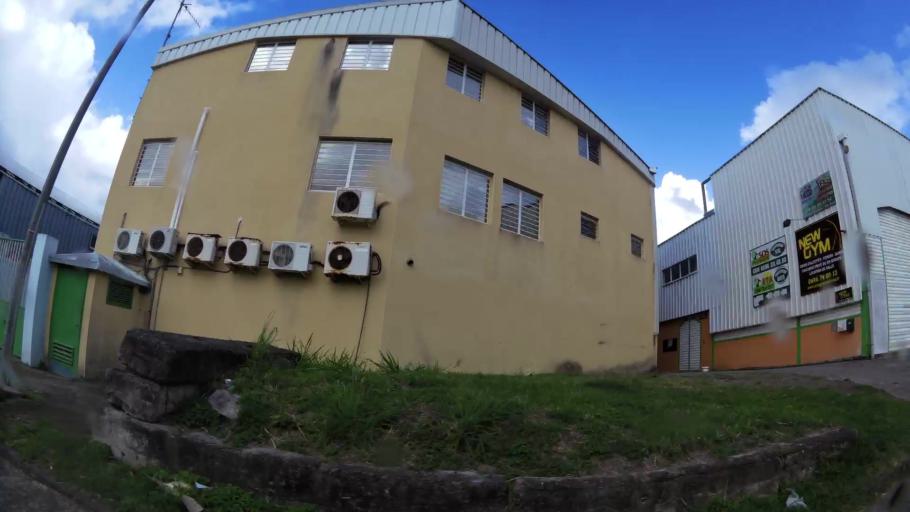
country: MQ
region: Martinique
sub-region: Martinique
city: Sainte-Luce
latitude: 14.4962
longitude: -60.9770
